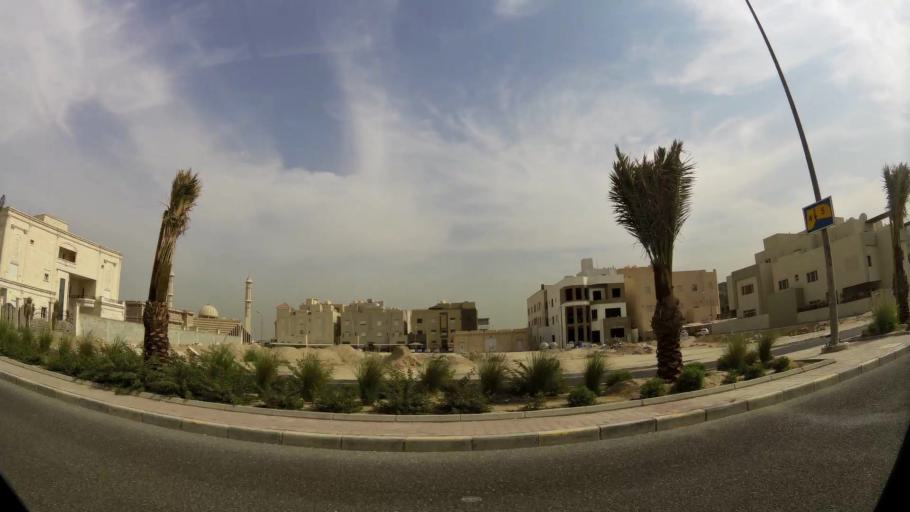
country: KW
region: Al Farwaniyah
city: Janub as Surrah
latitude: 29.2919
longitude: 47.9924
